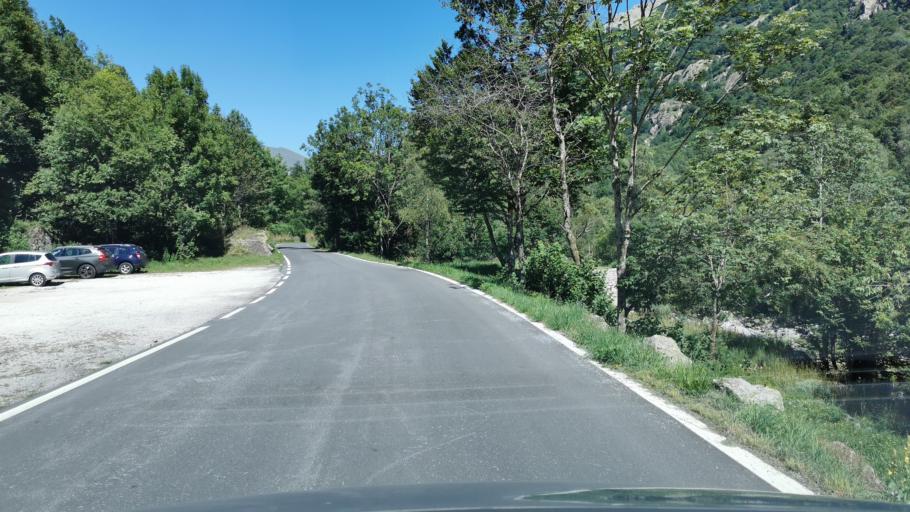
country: IT
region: Piedmont
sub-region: Provincia di Cuneo
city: Demonte
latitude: 44.2282
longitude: 7.3073
